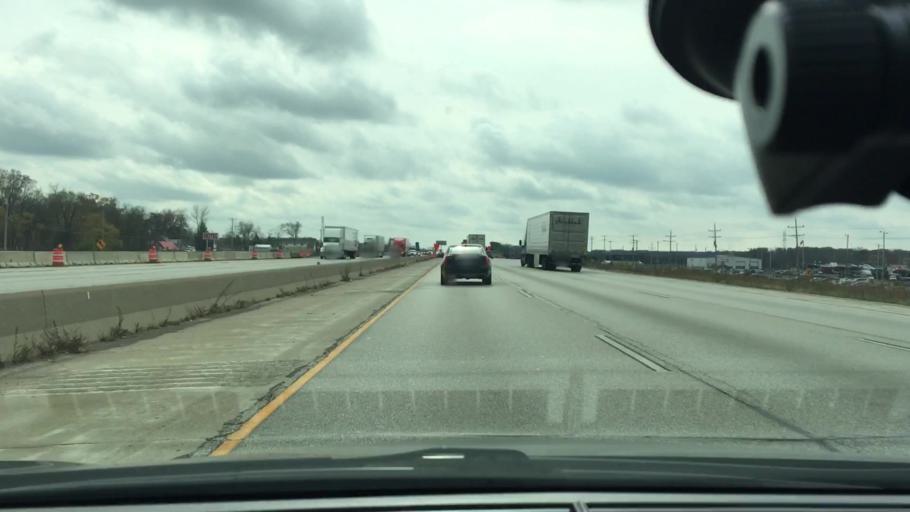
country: US
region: Wisconsin
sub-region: Racine County
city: Caledonia
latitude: 42.8355
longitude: -87.9526
